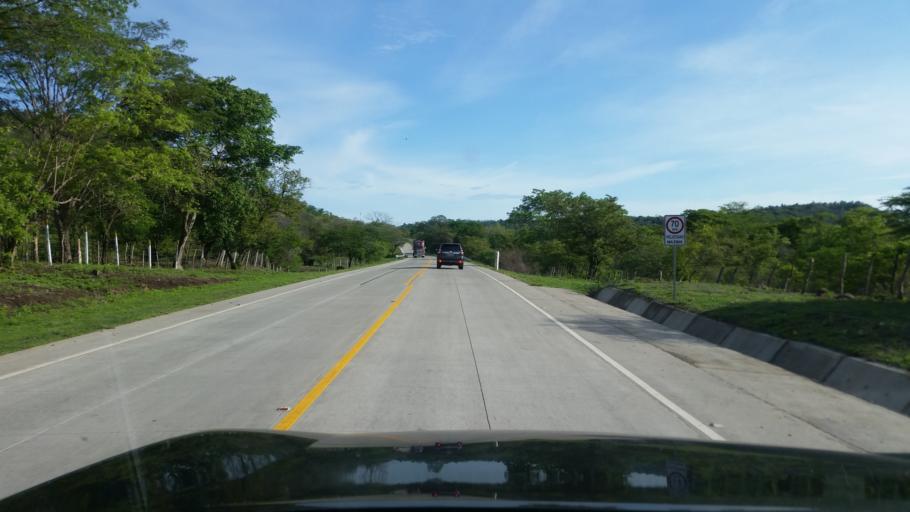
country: NI
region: Leon
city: Nagarote
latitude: 12.1530
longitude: -86.6544
